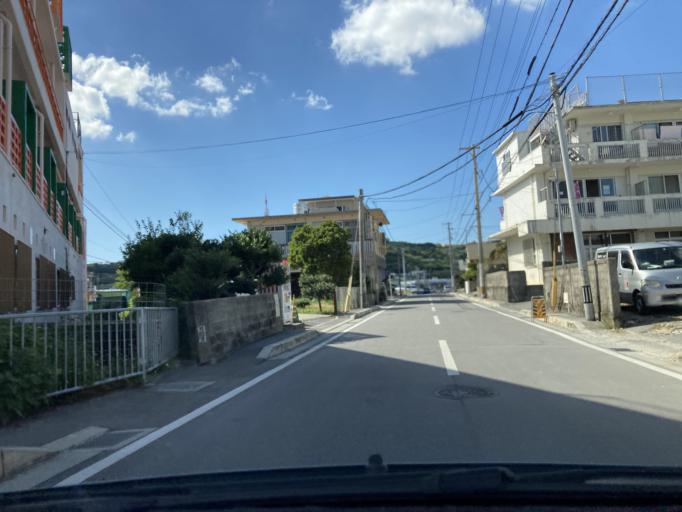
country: JP
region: Okinawa
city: Tomigusuku
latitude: 26.1878
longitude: 127.7120
